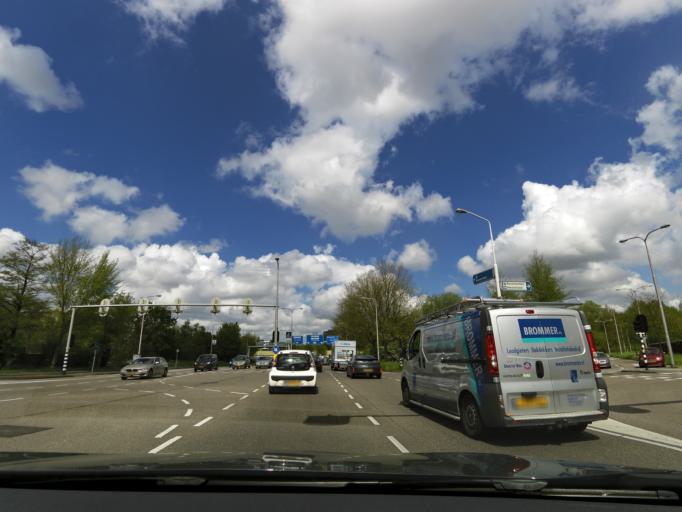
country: NL
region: North Holland
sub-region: Gemeente Amstelveen
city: Amstelveen
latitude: 52.2996
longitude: 4.8551
